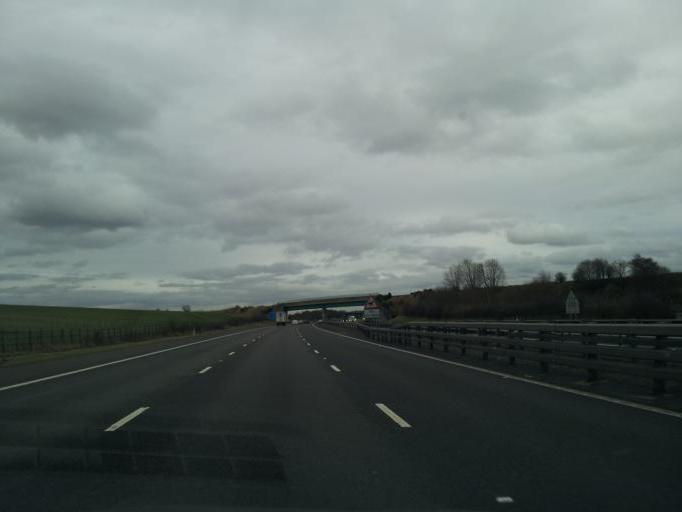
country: GB
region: England
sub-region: Staffordshire
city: Chasetown
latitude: 52.6598
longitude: -1.9126
